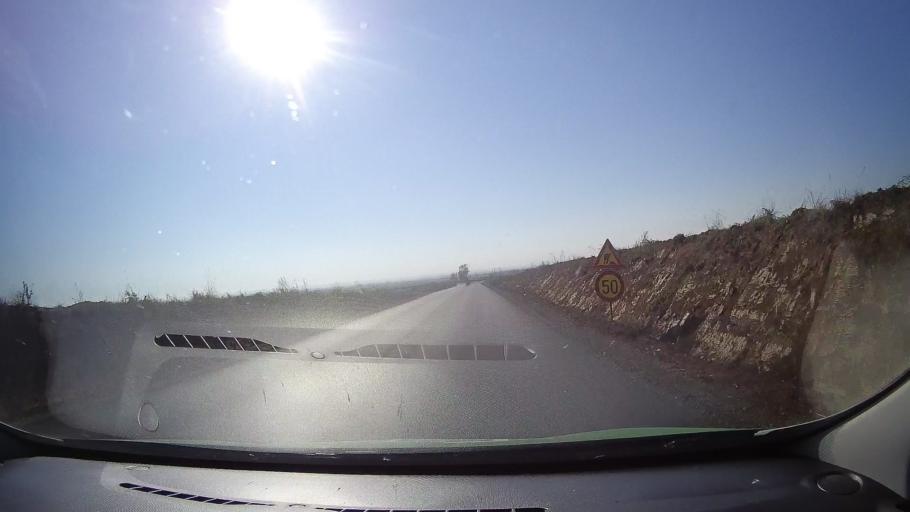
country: RO
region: Satu Mare
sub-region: Comuna Tiream
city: Tiream
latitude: 47.6448
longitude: 22.4639
